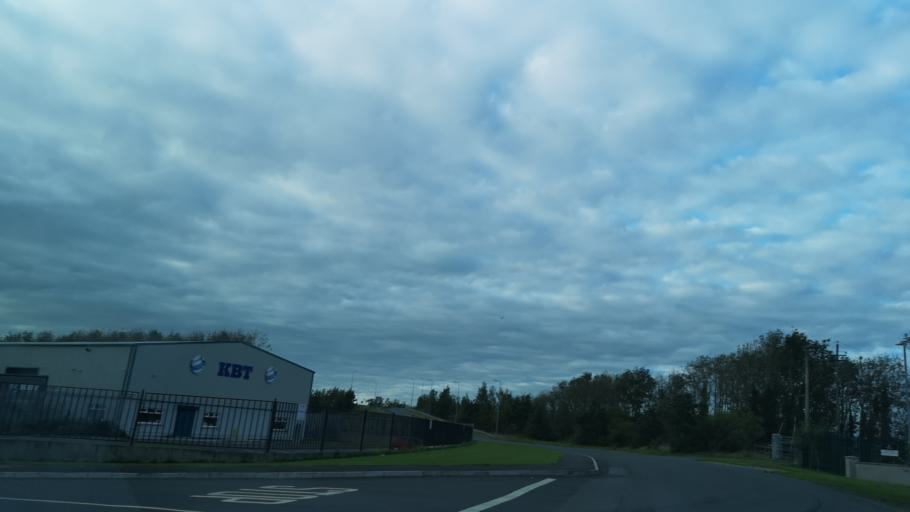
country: IE
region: Connaught
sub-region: County Galway
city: Athenry
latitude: 53.2876
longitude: -8.7550
